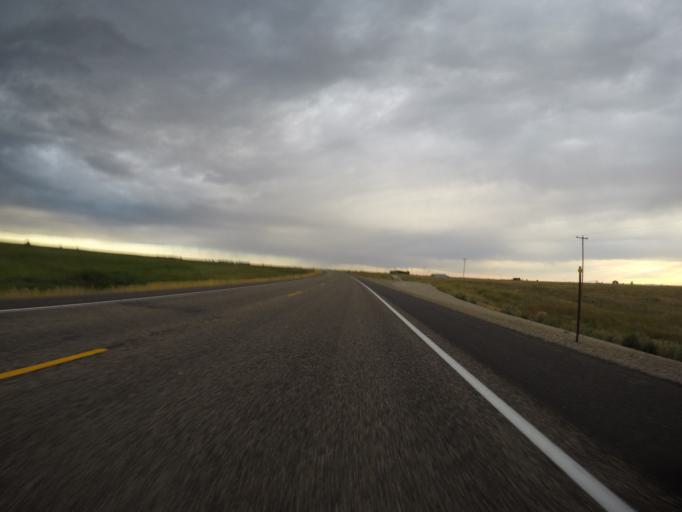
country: US
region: Wyoming
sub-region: Albany County
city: Laramie
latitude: 41.7649
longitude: -105.9756
